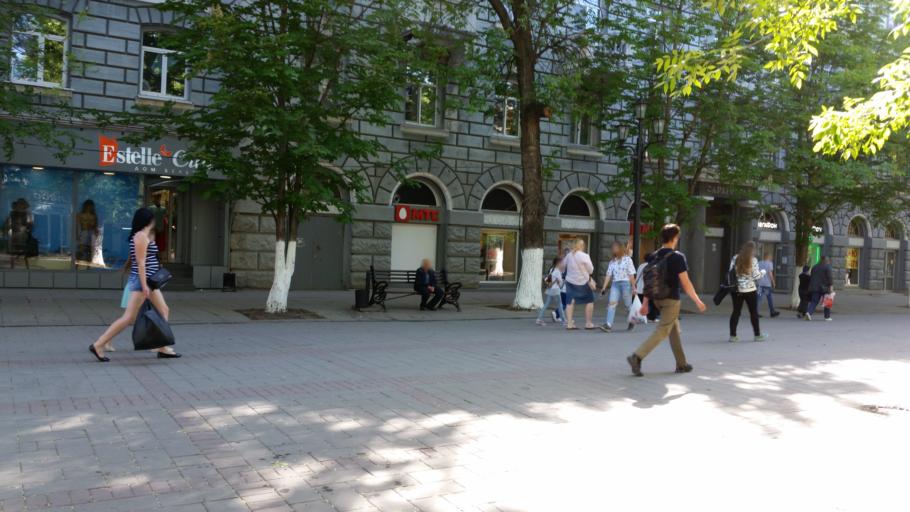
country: RU
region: Saratov
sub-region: Saratovskiy Rayon
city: Saratov
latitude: 51.5313
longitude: 46.0288
